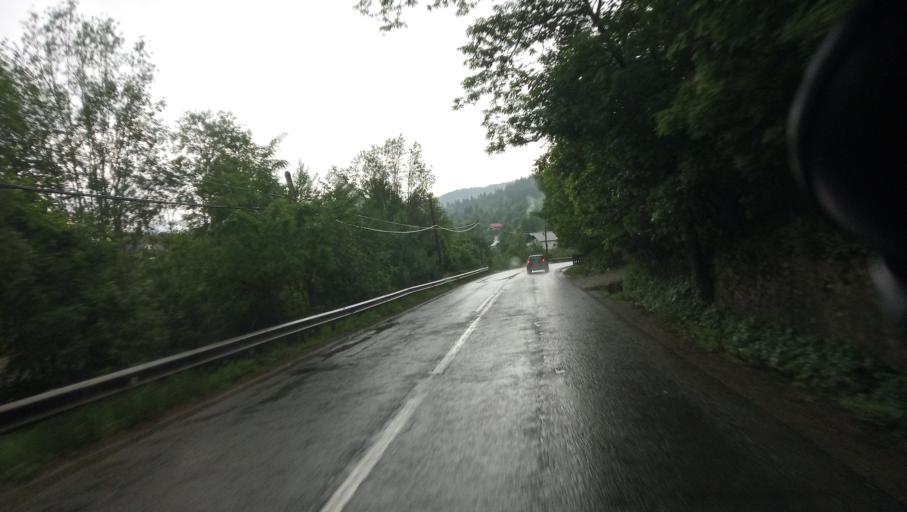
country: RO
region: Neamt
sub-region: Comuna Poiana Teiului
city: Poiana Teiului
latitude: 47.0965
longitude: 25.9826
